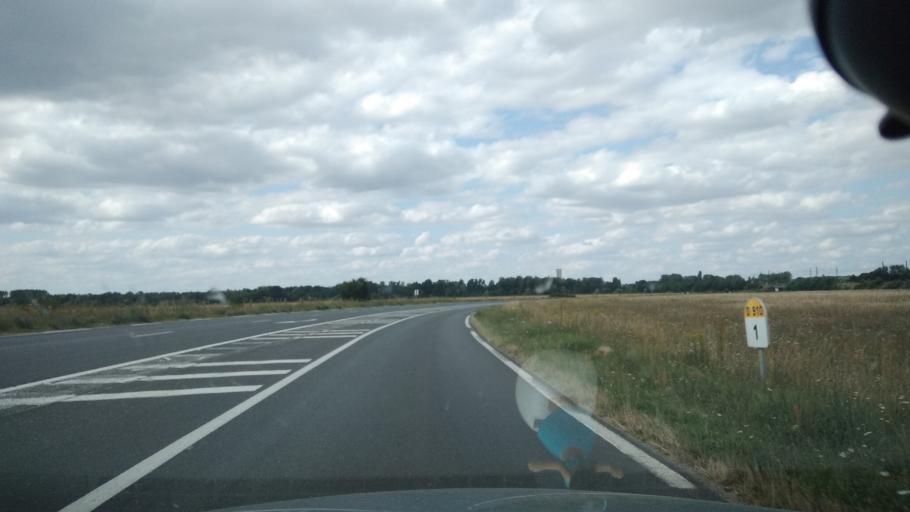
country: FR
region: Centre
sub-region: Departement d'Indre-et-Loire
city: La Celle-Saint-Avant
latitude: 46.9986
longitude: 0.5943
